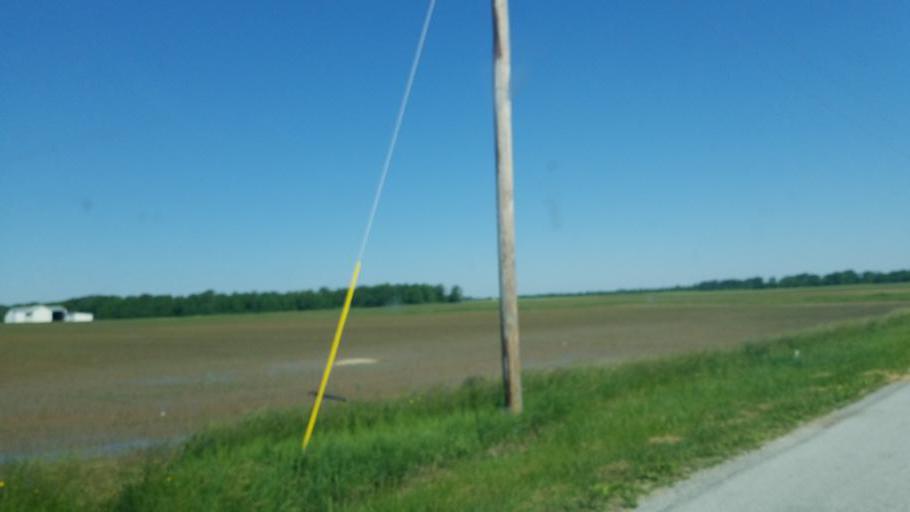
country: US
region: Ohio
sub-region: Hardin County
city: Kenton
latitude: 40.6437
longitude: -83.6563
